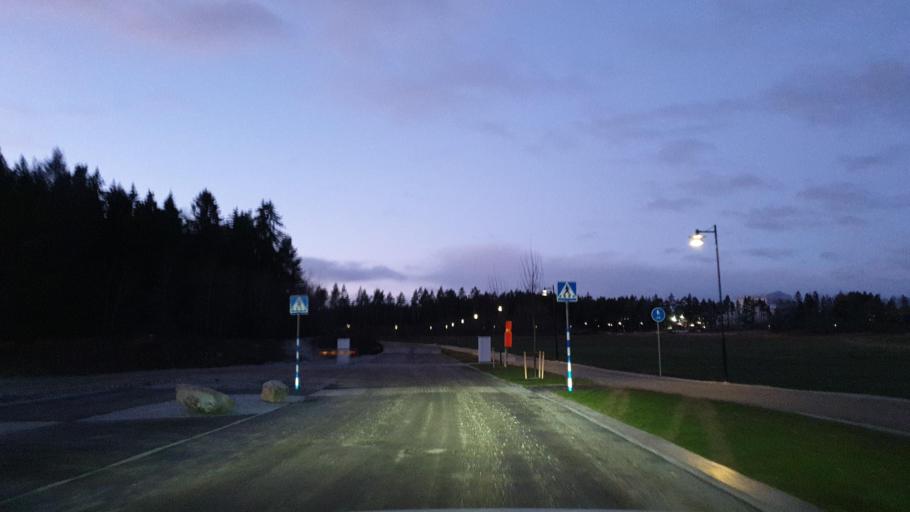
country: SE
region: Stockholm
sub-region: Sigtuna Kommun
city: Marsta
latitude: 59.6153
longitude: 17.7954
